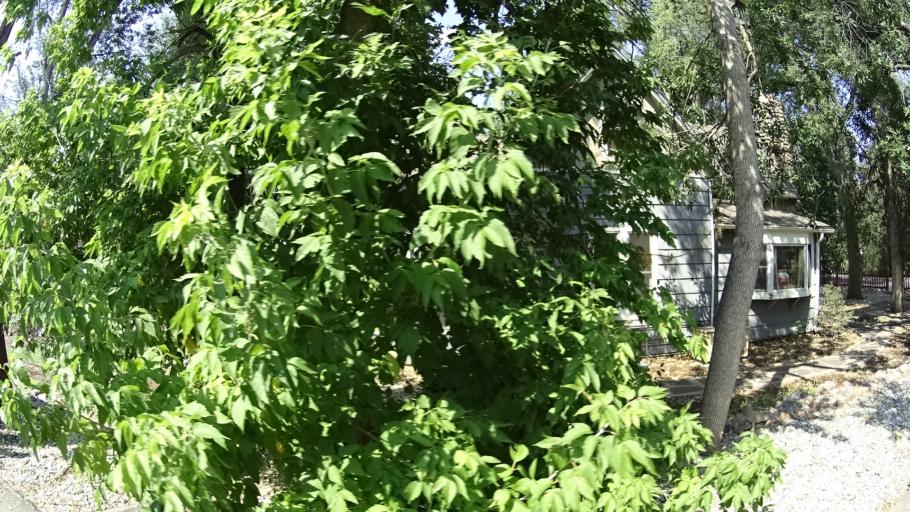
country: US
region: Colorado
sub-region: El Paso County
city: Colorado Springs
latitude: 38.8055
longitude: -104.8284
